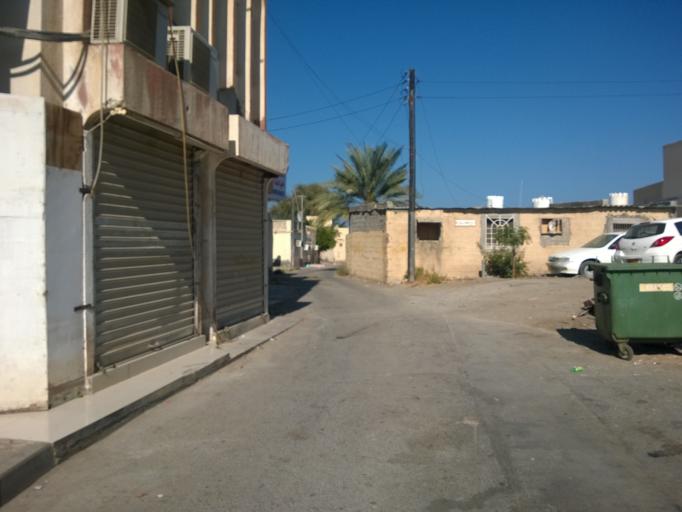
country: OM
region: Muhafazat Masqat
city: As Sib al Jadidah
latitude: 23.6767
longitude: 58.1907
